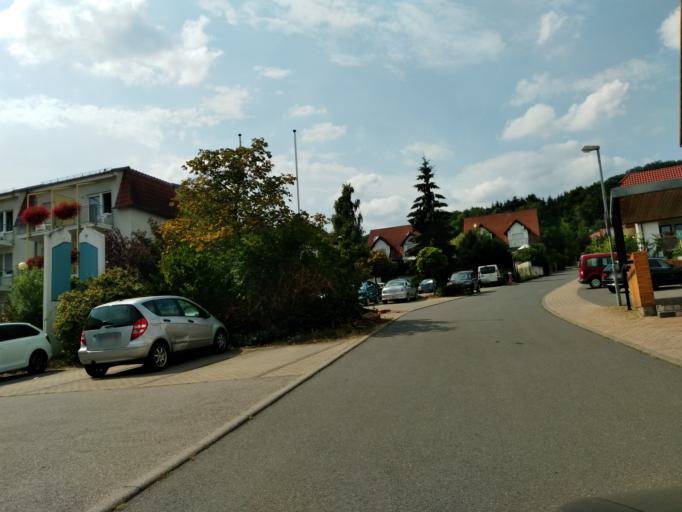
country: DE
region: Baden-Wuerttemberg
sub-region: Karlsruhe Region
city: Limbach
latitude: 49.4633
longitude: 9.2085
